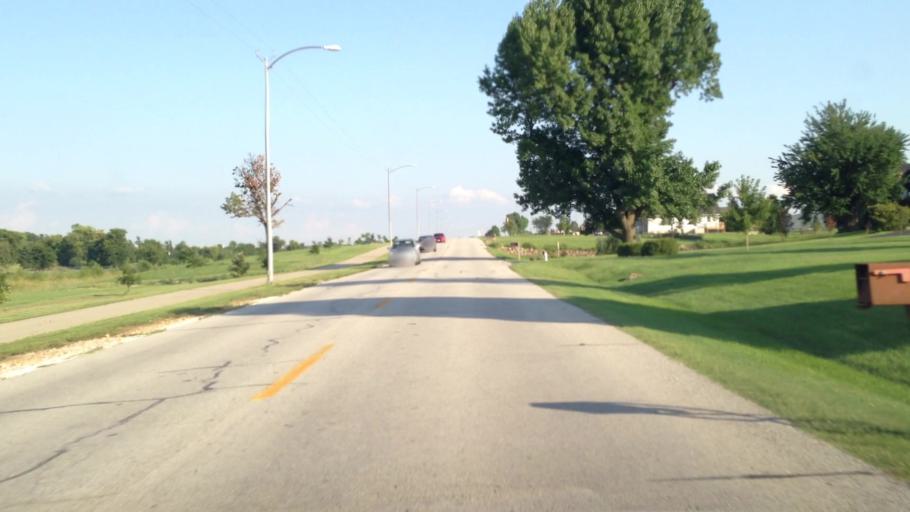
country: US
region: Missouri
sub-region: Jasper County
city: Joplin
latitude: 37.0737
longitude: -94.4899
